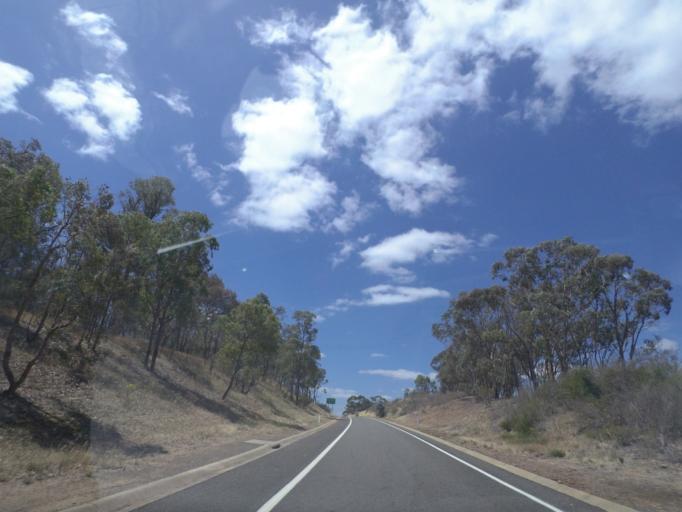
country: AU
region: Victoria
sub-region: Wangaratta
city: Wangaratta
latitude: -36.4681
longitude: 146.2079
